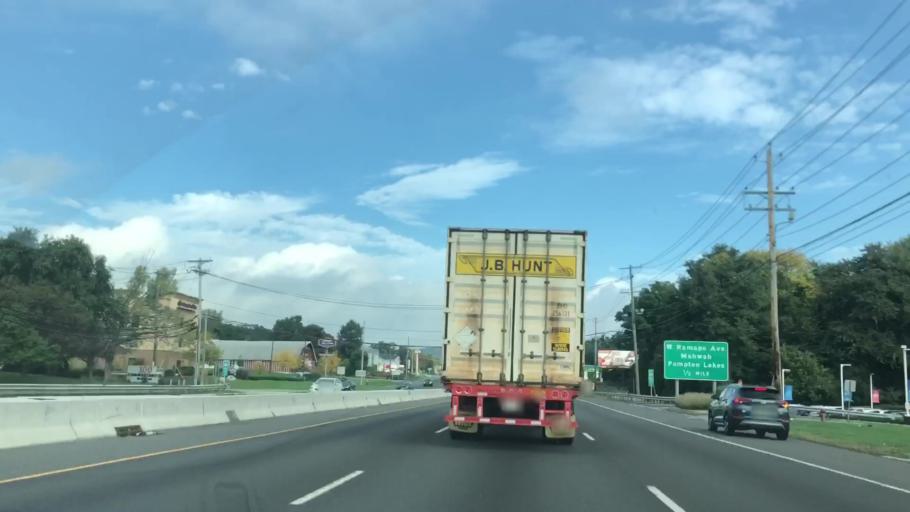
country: US
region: New Jersey
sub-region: Bergen County
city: Mahwah
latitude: 41.0884
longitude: -74.1530
